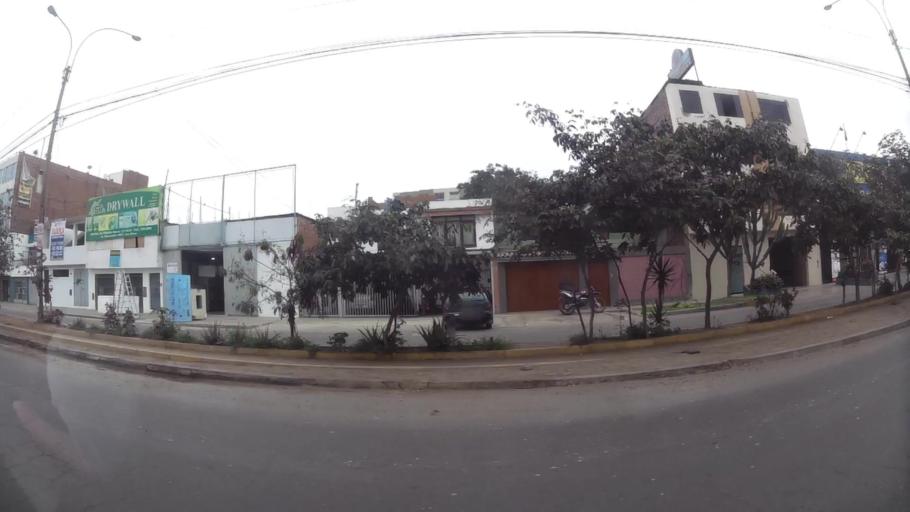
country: PE
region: Lima
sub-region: Lima
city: Independencia
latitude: -11.9798
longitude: -77.0785
